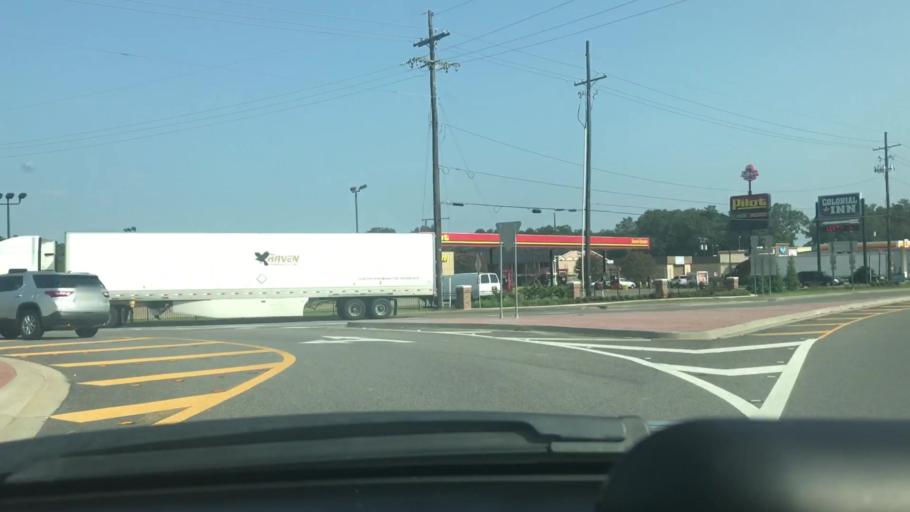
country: US
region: Louisiana
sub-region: Tangipahoa Parish
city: Hammond
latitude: 30.4777
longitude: -90.4570
